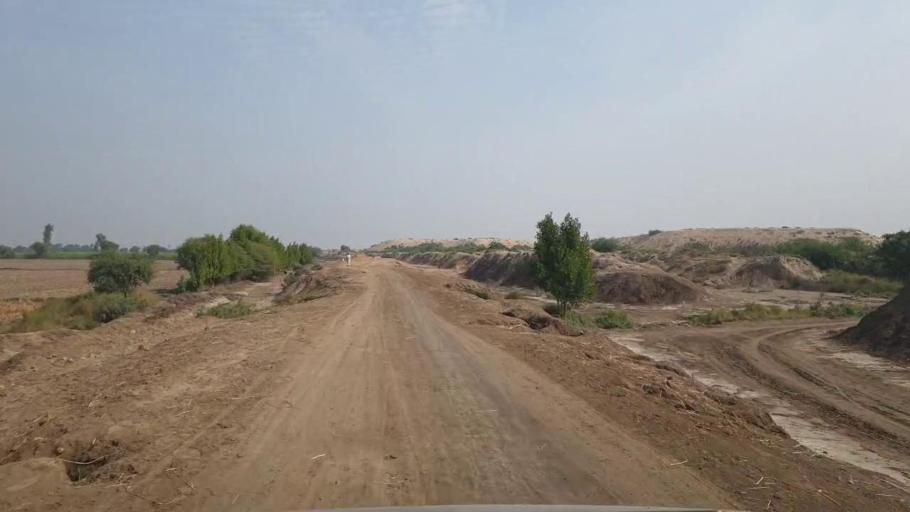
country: PK
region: Sindh
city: Tando Muhammad Khan
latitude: 25.1516
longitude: 68.4633
